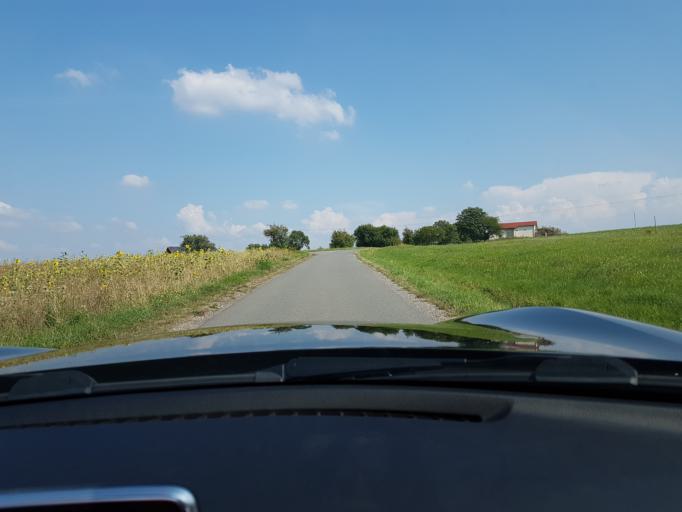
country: DE
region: Baden-Wuerttemberg
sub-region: Karlsruhe Region
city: Osterburken
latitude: 49.4308
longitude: 9.4438
